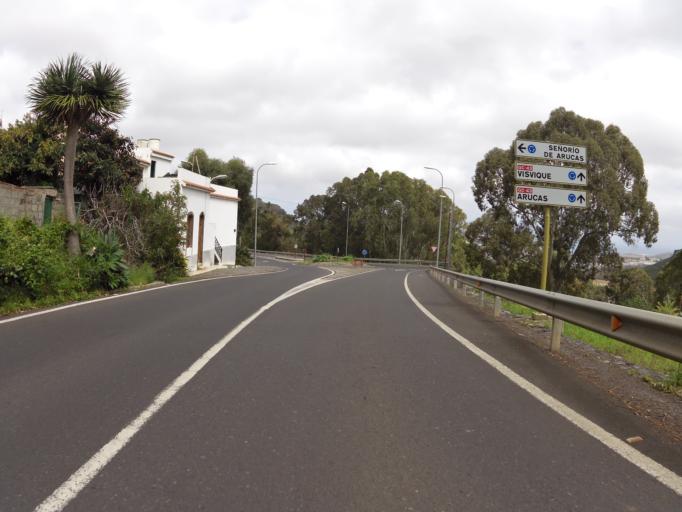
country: ES
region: Canary Islands
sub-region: Provincia de Las Palmas
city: Arucas
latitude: 28.0965
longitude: -15.5319
